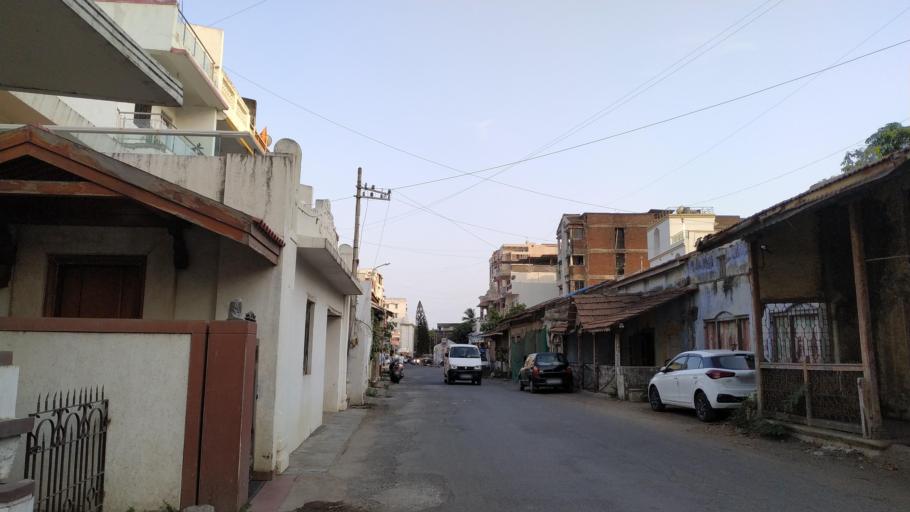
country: IN
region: Daman and Diu
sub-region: Daman District
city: Daman
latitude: 20.4164
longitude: 72.8335
